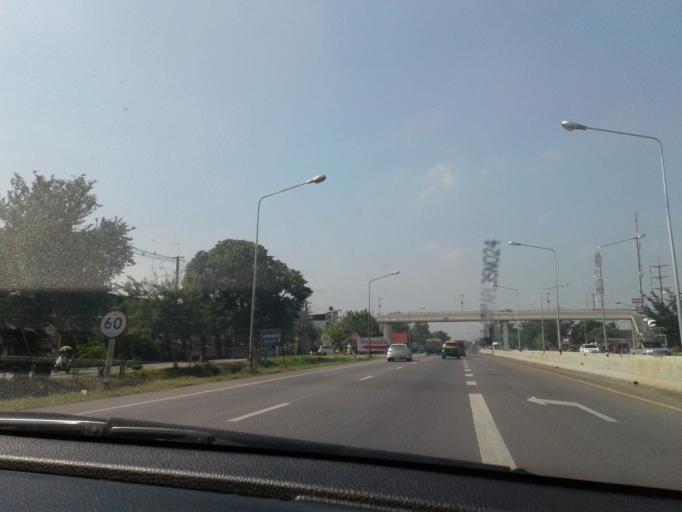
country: TH
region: Ratchaburi
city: Bang Phae
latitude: 13.7398
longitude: 99.9162
